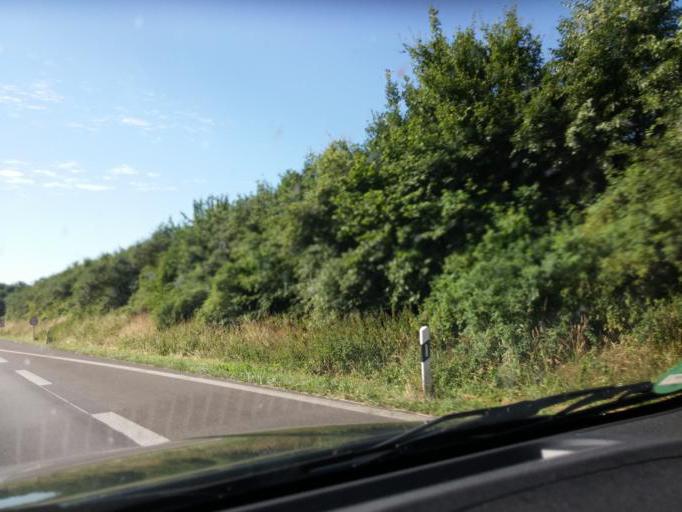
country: DE
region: North Rhine-Westphalia
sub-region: Regierungsbezirk Dusseldorf
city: Monchengladbach
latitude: 51.1857
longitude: 6.3905
